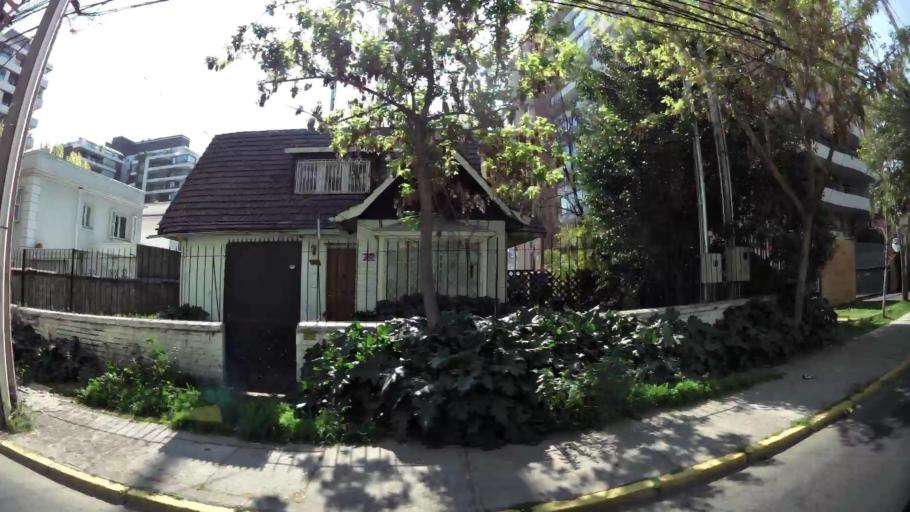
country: CL
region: Santiago Metropolitan
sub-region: Provincia de Santiago
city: Villa Presidente Frei, Nunoa, Santiago, Chile
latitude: -33.4036
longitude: -70.5926
